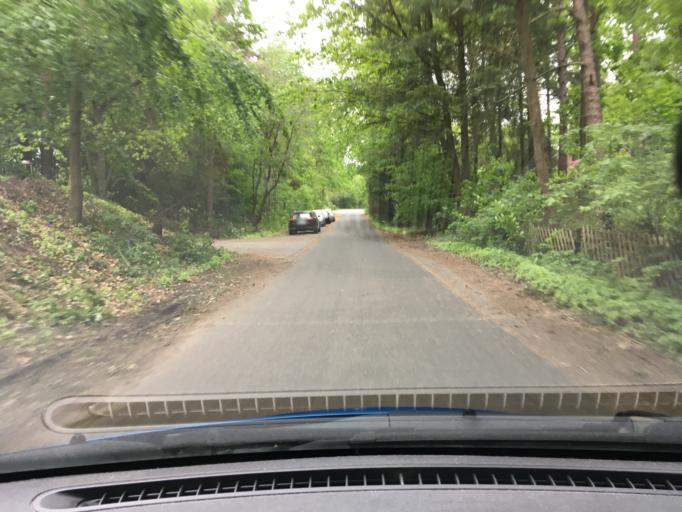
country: DE
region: Lower Saxony
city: Bispingen
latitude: 53.0696
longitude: 10.0086
